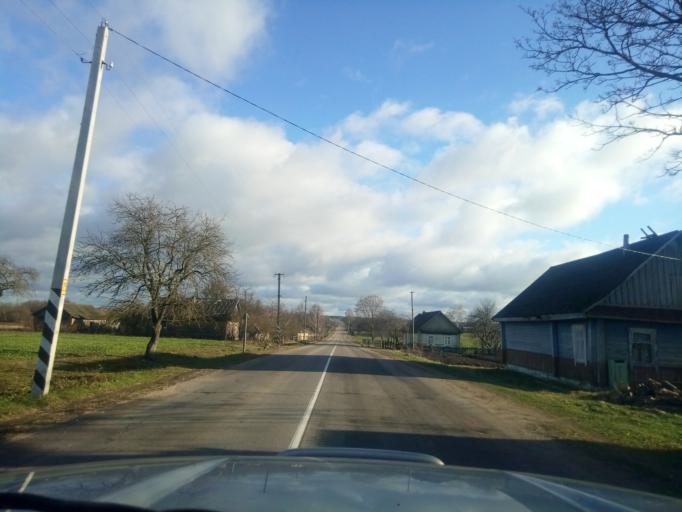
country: BY
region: Minsk
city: Tsimkavichy
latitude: 53.1761
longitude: 26.9470
